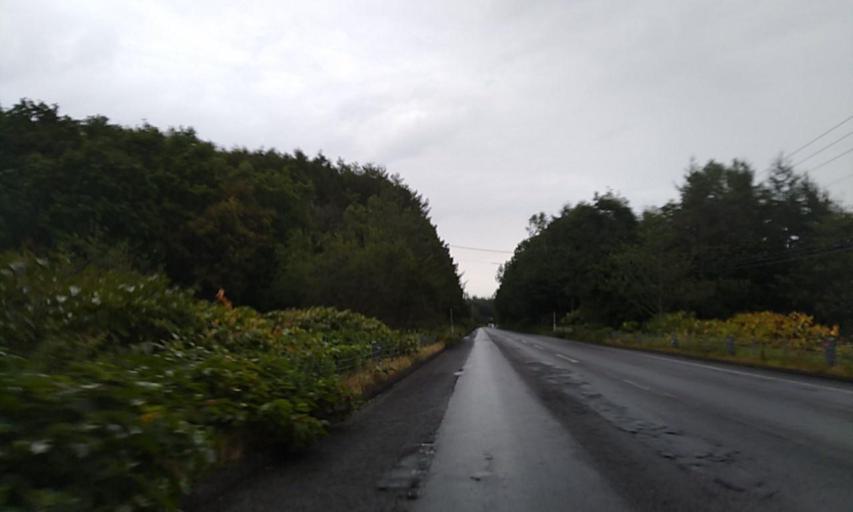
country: JP
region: Hokkaido
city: Mombetsu
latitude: 44.4814
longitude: 143.1059
